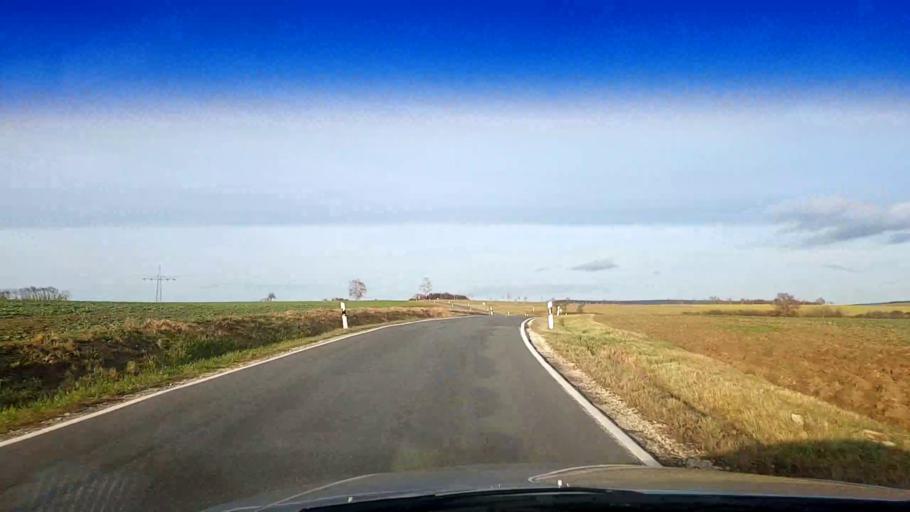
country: DE
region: Bavaria
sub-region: Upper Franconia
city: Strullendorf
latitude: 49.8464
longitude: 11.0009
